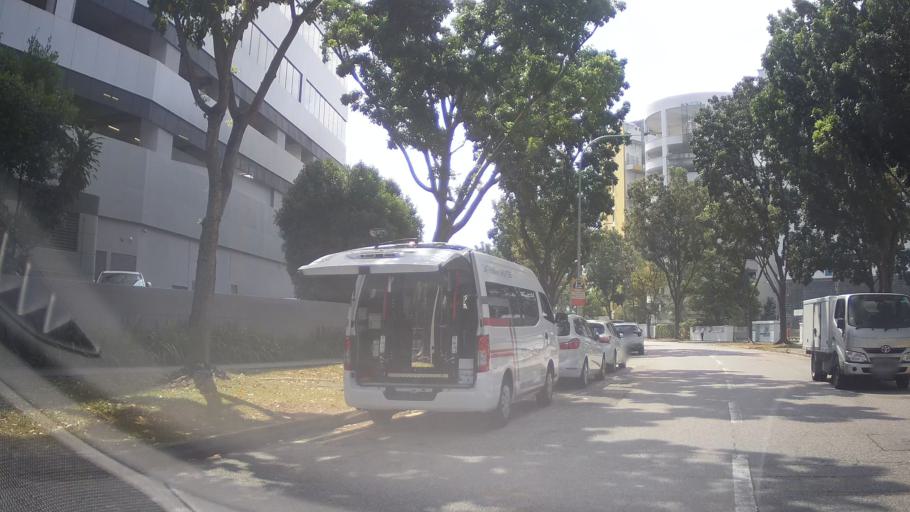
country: SG
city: Singapore
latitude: 1.3126
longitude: 103.8661
